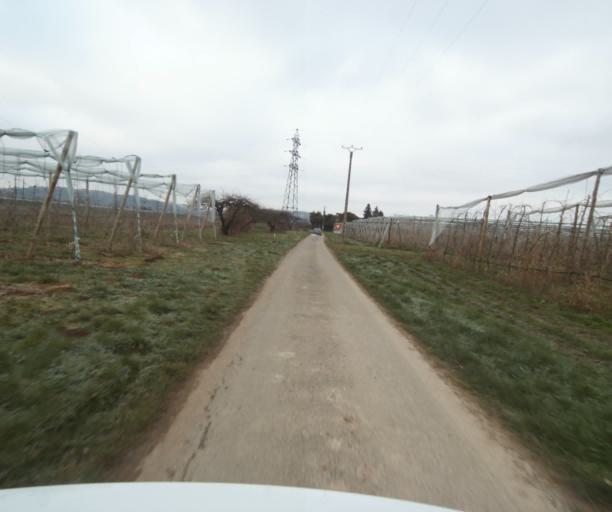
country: FR
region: Midi-Pyrenees
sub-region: Departement du Tarn-et-Garonne
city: Moissac
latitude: 44.1063
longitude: 1.1335
